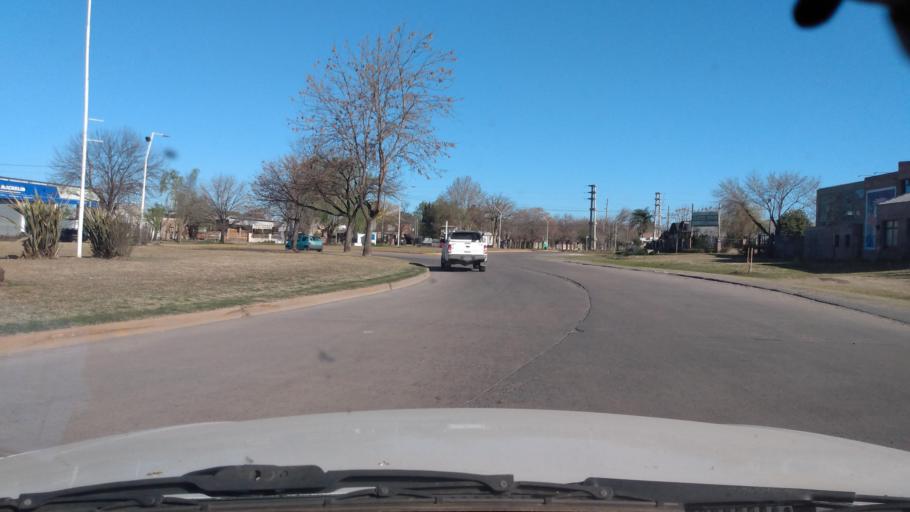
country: AR
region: Buenos Aires
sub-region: Partido de Mercedes
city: Mercedes
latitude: -34.6475
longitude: -59.4168
